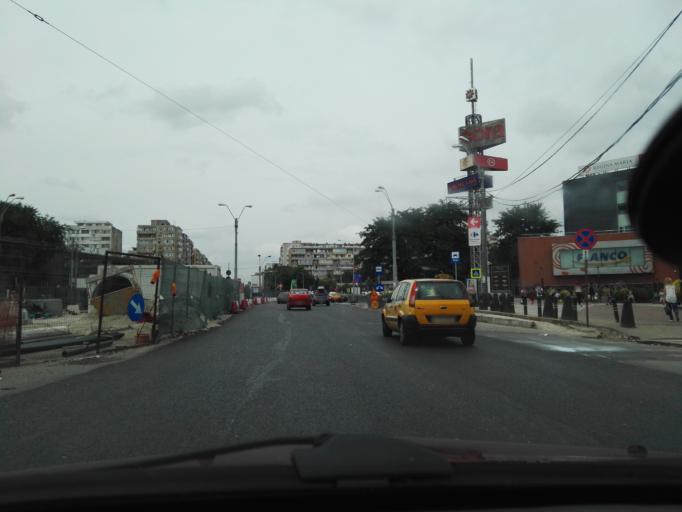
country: RO
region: Bucuresti
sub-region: Municipiul Bucuresti
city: Bucharest
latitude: 44.3934
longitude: 26.1223
